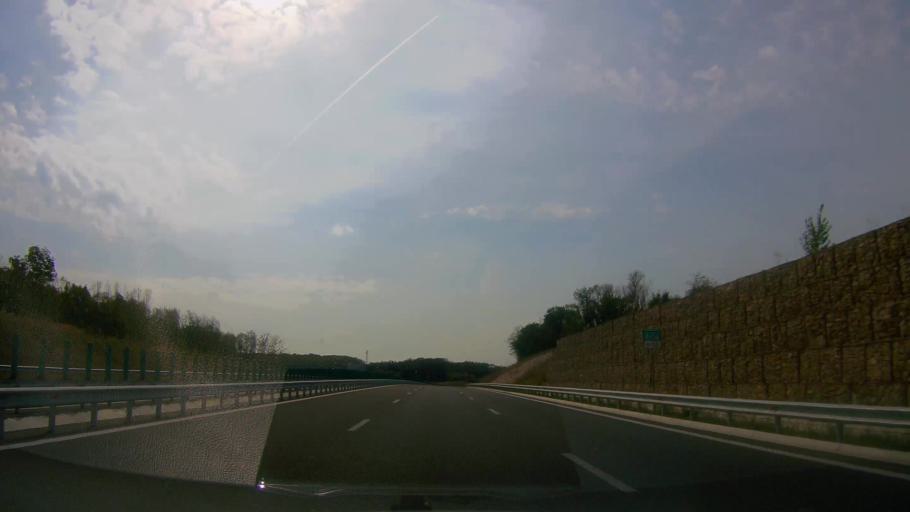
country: RO
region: Cluj
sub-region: Comuna Baciu
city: Mera
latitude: 46.7893
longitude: 23.4163
